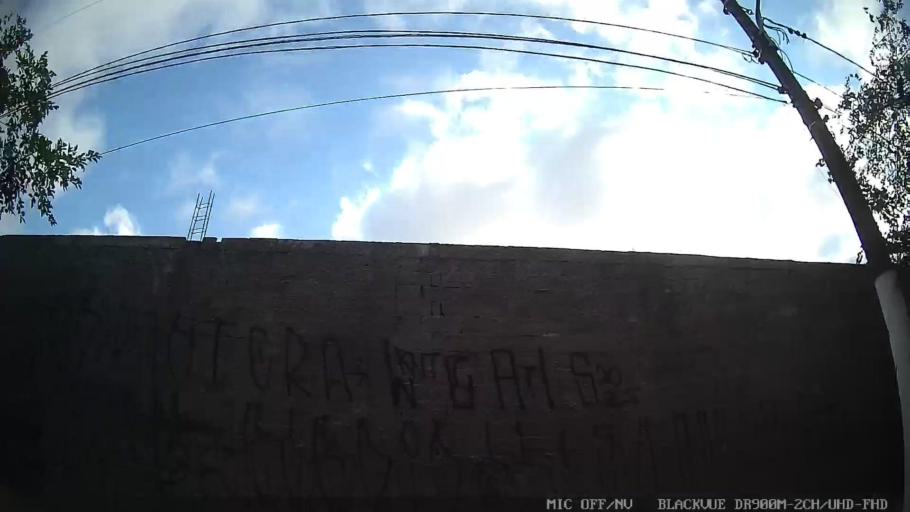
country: BR
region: Sao Paulo
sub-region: Guarulhos
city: Guarulhos
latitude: -23.5401
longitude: -46.5147
